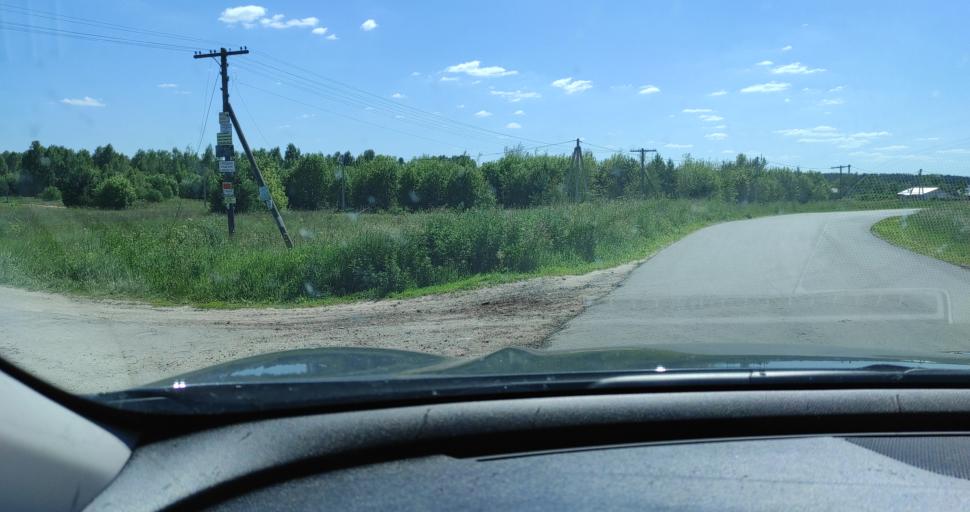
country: RU
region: Rjazan
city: Murmino
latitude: 54.5677
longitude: 40.0950
